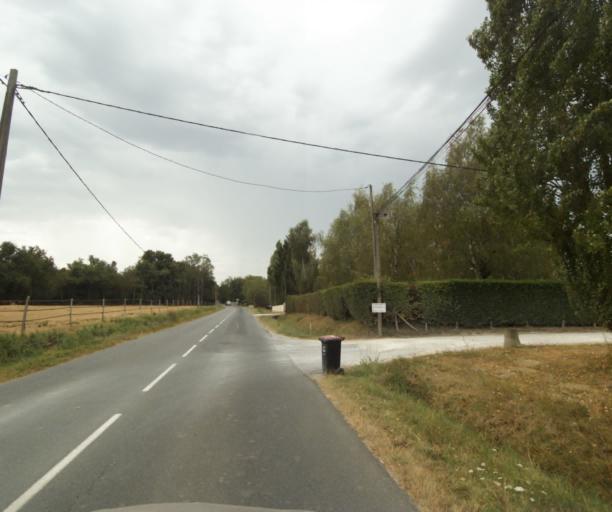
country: FR
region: Aquitaine
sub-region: Departement de la Gironde
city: La Sauve
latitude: 44.7632
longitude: -0.3317
